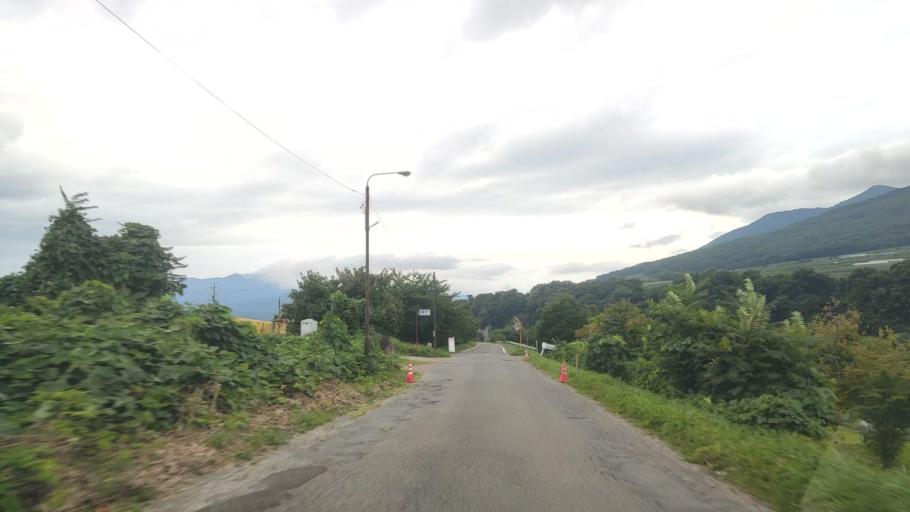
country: JP
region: Nagano
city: Nakano
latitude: 36.7658
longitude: 138.3934
